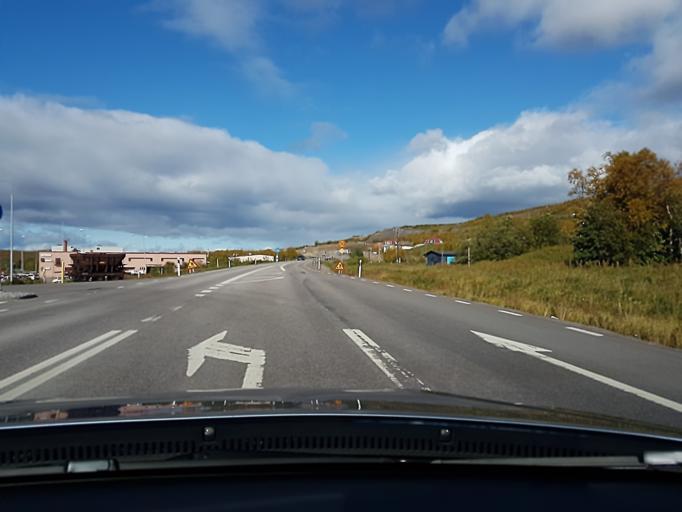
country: SE
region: Norrbotten
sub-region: Kiruna Kommun
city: Kiruna
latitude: 67.8667
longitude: 20.2024
